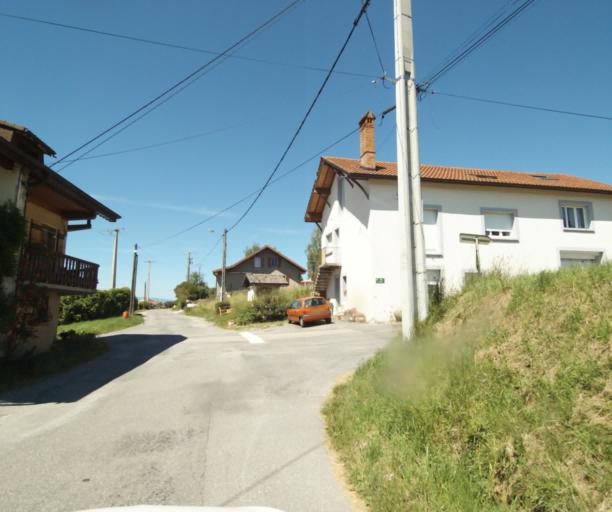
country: FR
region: Rhone-Alpes
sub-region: Departement de la Haute-Savoie
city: Ballaison
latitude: 46.2863
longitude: 6.3251
